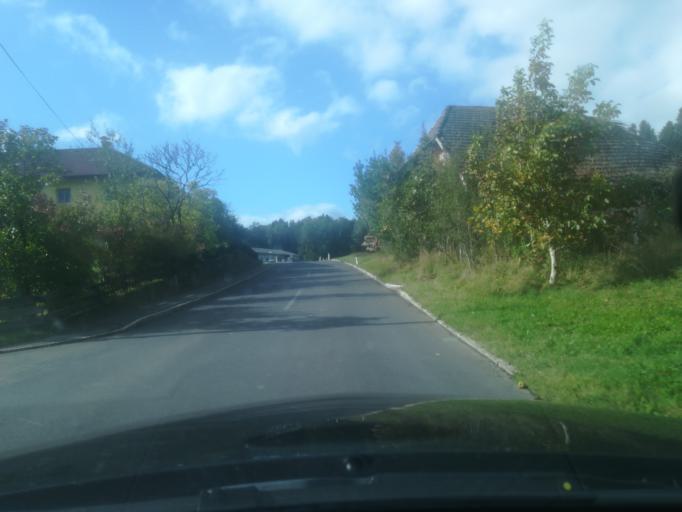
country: AT
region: Upper Austria
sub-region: Politischer Bezirk Urfahr-Umgebung
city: Herzogsdorf
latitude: 48.4300
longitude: 14.1230
